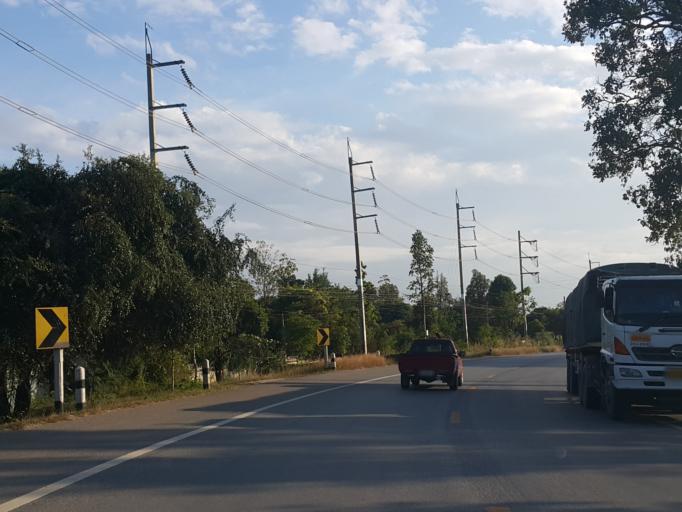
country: TH
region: Lampang
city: Lampang
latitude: 18.4509
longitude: 99.5399
